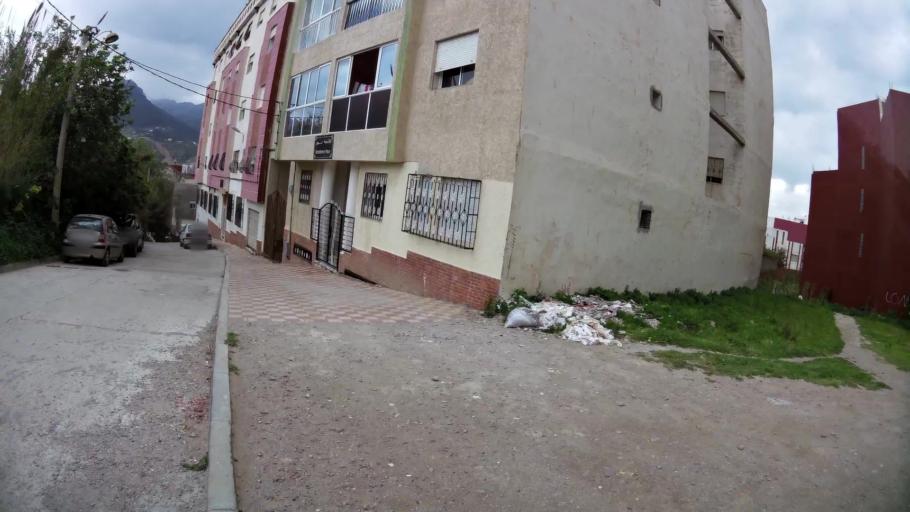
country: MA
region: Tanger-Tetouan
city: Tetouan
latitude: 35.5671
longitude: -5.3785
